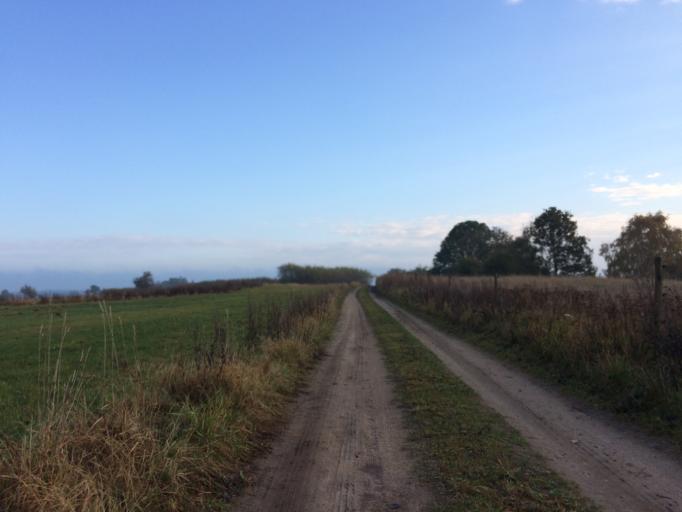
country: DK
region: Zealand
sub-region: Ringsted Kommune
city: Ringsted
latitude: 55.4869
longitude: 11.7494
